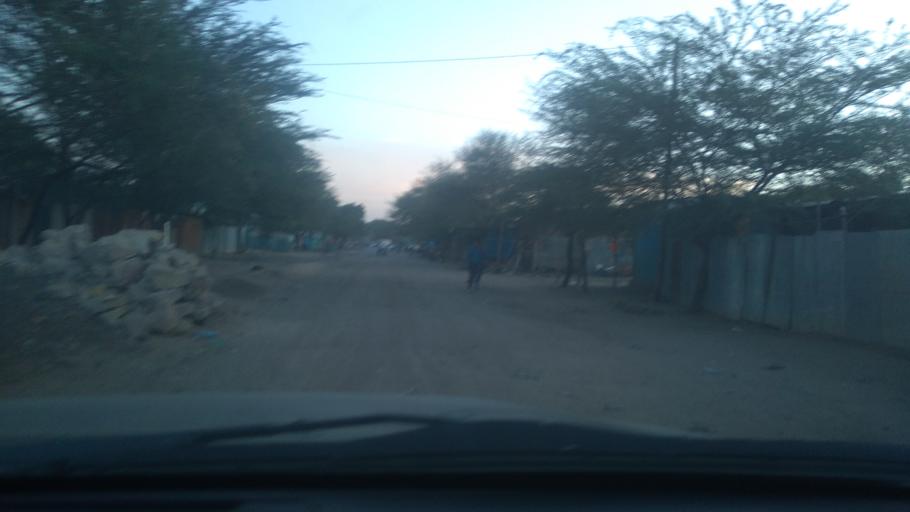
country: ET
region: Oromiya
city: Asbe Teferi
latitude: 9.2351
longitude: 40.7568
